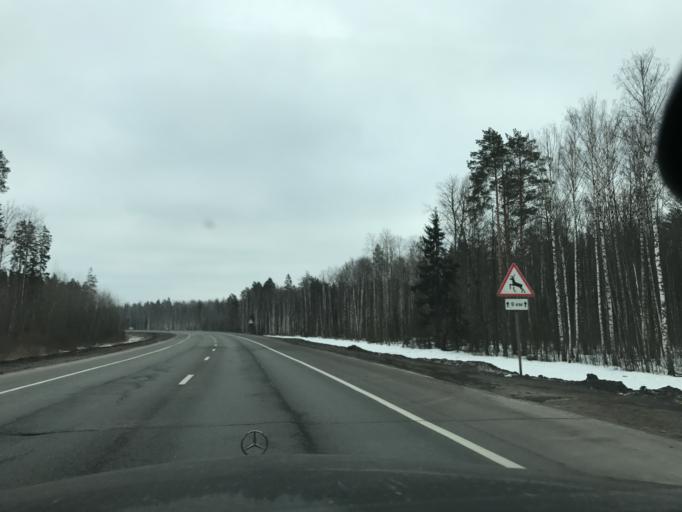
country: RU
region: Vladimir
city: Raduzhnyy
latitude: 56.0729
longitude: 40.2211
